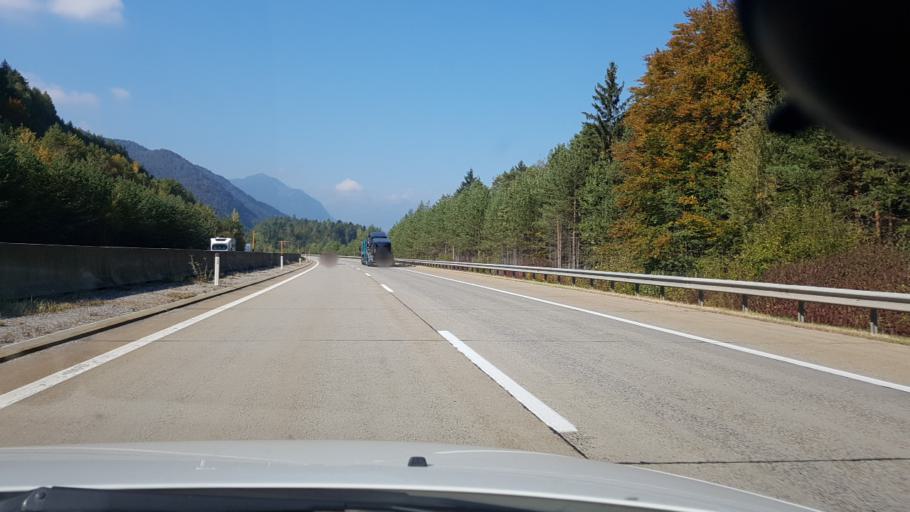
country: AT
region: Carinthia
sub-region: Politischer Bezirk Villach Land
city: Fresach
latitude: 46.6795
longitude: 13.6864
